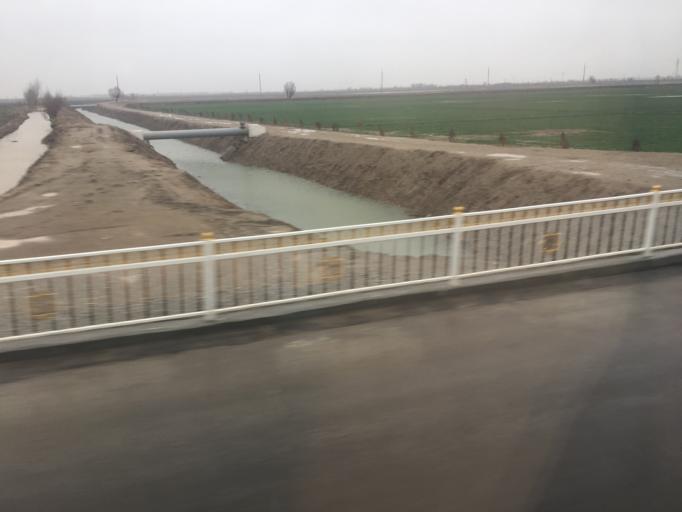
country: TM
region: Lebap
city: Turkmenabat
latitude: 39.0001
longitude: 63.5890
